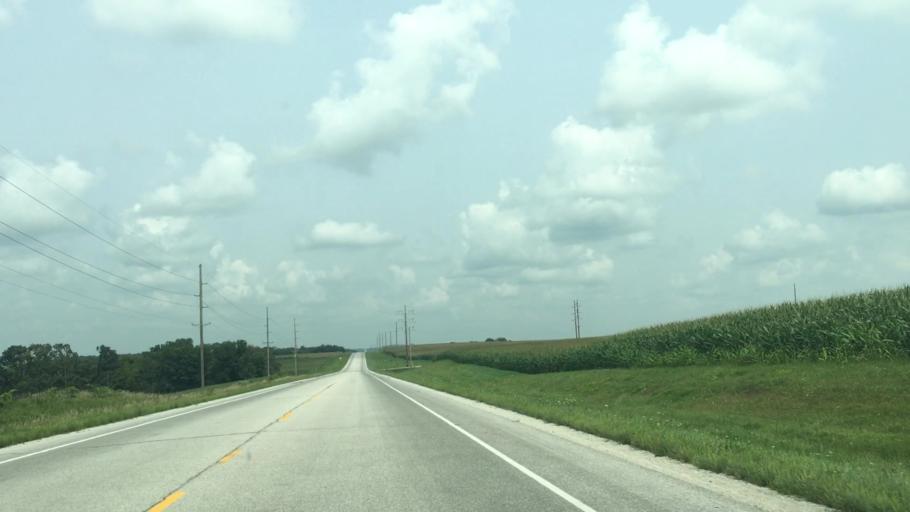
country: US
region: Minnesota
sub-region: Fillmore County
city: Harmony
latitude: 43.5633
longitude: -91.9297
